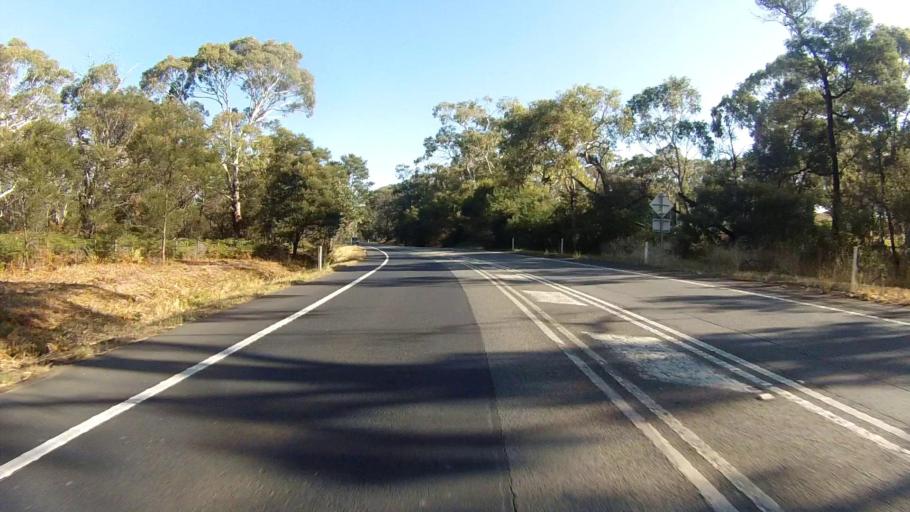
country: AU
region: Tasmania
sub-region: Clarence
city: Seven Mile Beach
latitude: -42.8157
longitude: 147.5116
